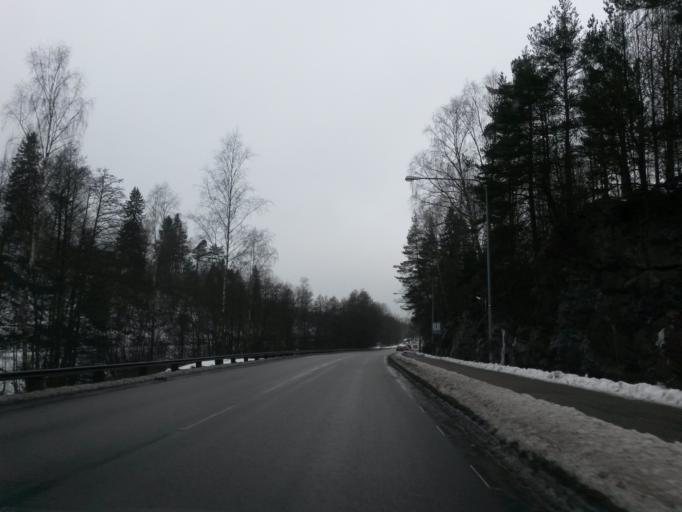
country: SE
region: Vaestra Goetaland
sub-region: Boras Kommun
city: Boras
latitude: 57.7052
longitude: 12.9618
